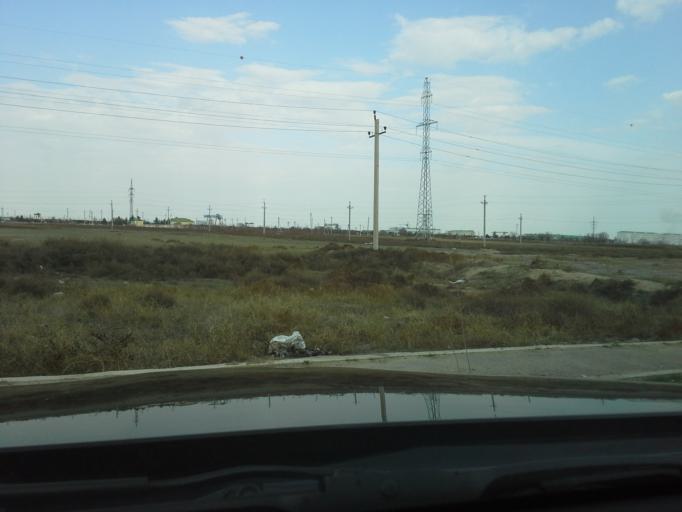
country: TM
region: Ahal
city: Ashgabat
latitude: 37.9936
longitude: 58.2994
